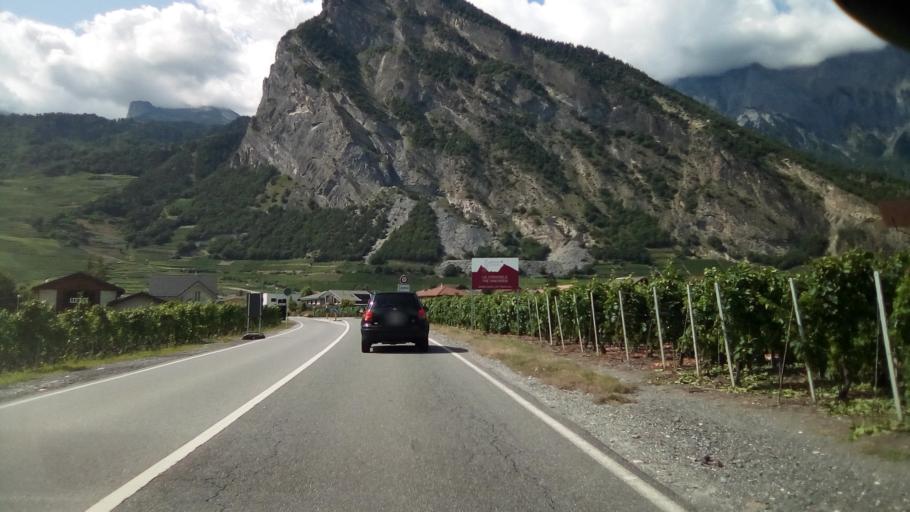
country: CH
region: Valais
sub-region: Martigny District
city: Leytron
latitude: 46.1831
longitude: 7.2149
